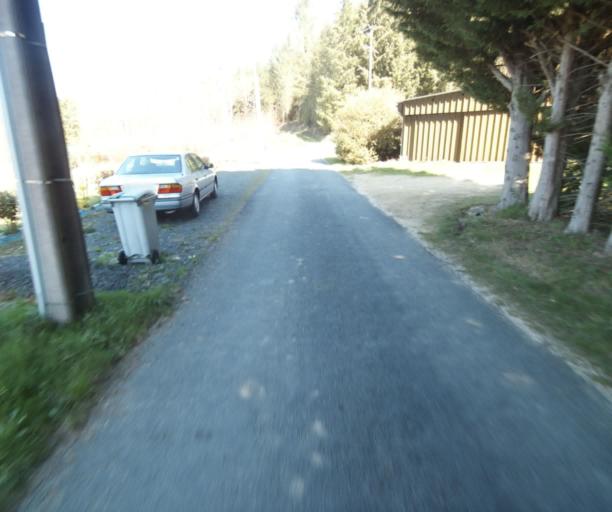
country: FR
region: Limousin
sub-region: Departement de la Correze
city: Saint-Mexant
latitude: 45.3107
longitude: 1.6224
